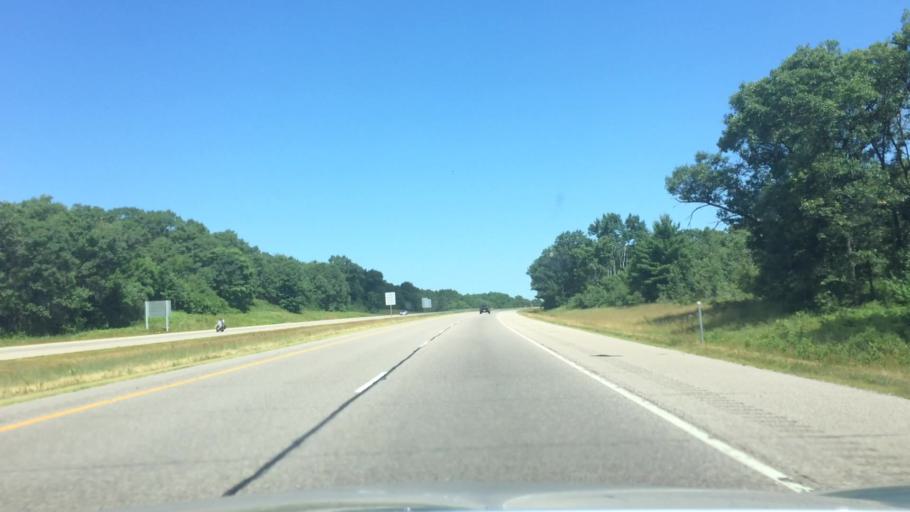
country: US
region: Wisconsin
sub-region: Marquette County
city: Westfield
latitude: 44.0481
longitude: -89.5393
